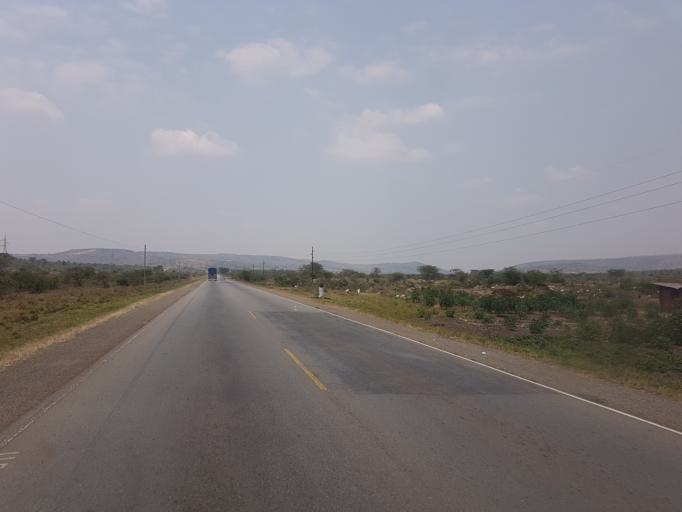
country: UG
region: Western Region
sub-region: Mbarara District
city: Mbarara
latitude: -0.5103
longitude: 30.8256
